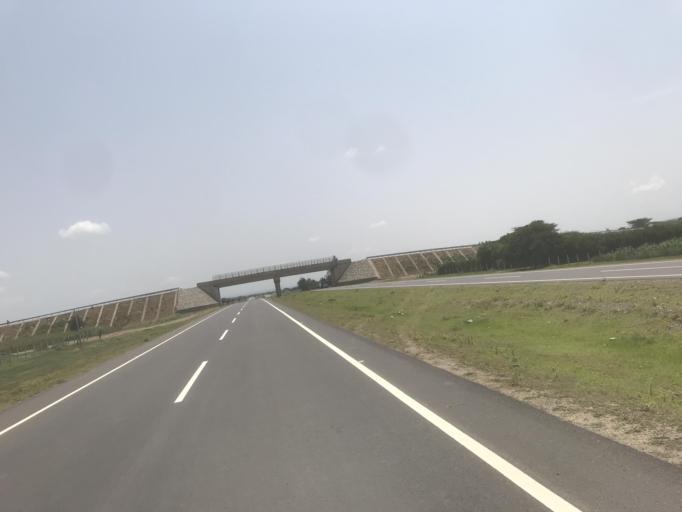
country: ET
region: Oromiya
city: Mojo
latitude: 8.2759
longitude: 38.9115
